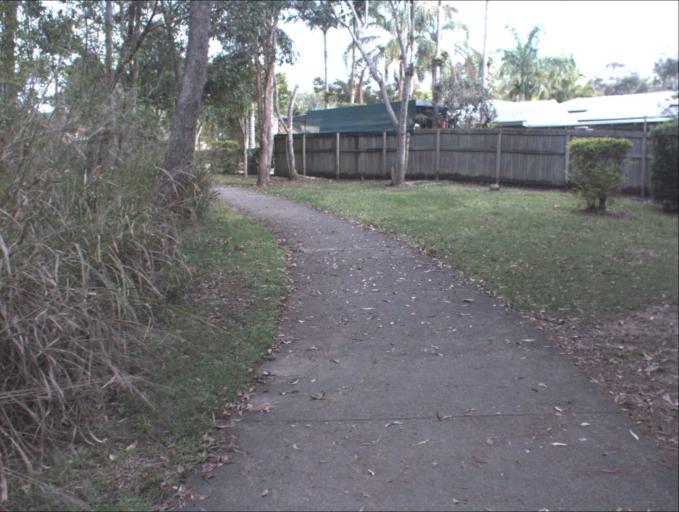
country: AU
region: Queensland
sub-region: Logan
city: Park Ridge South
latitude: -27.6859
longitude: 153.0395
